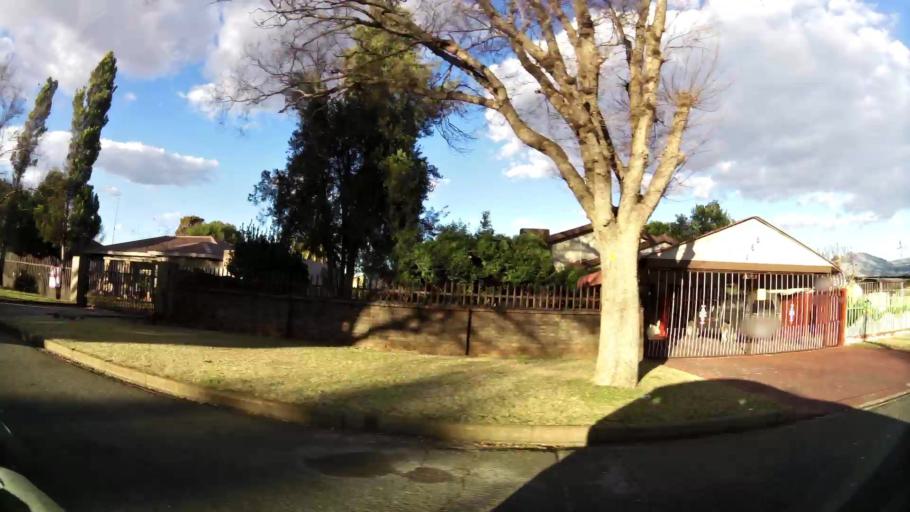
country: ZA
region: North-West
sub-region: Dr Kenneth Kaunda District Municipality
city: Potchefstroom
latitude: -26.7235
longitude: 27.1004
